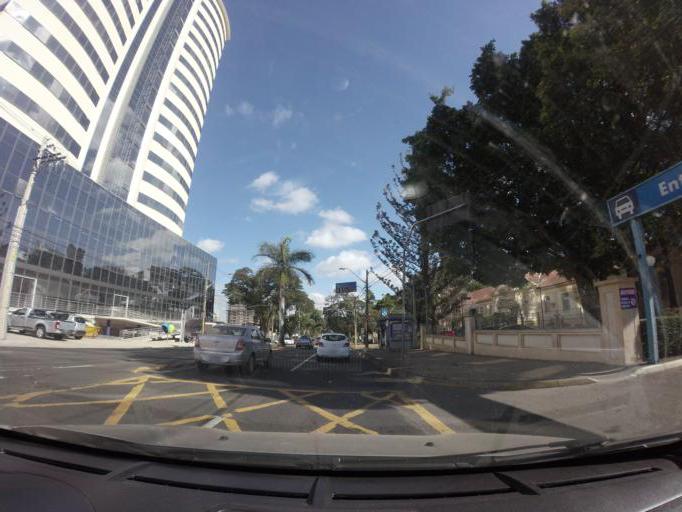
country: BR
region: Sao Paulo
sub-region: Piracicaba
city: Piracicaba
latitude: -22.7378
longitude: -47.6432
